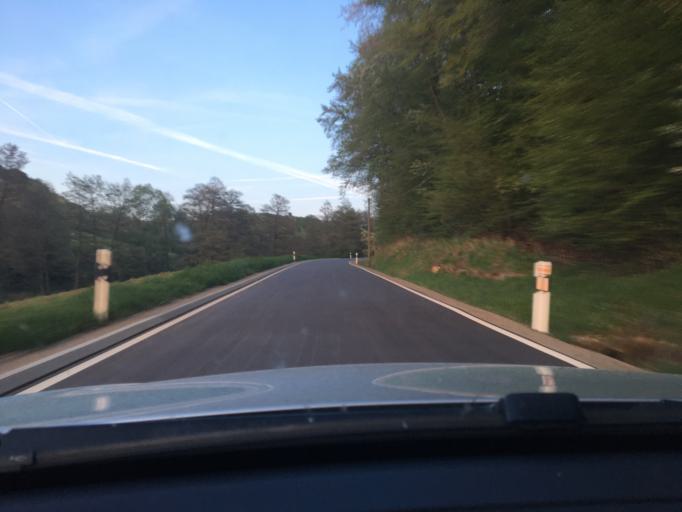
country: DE
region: Rheinland-Pfalz
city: Munsterappel
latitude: 49.7145
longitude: 7.8921
